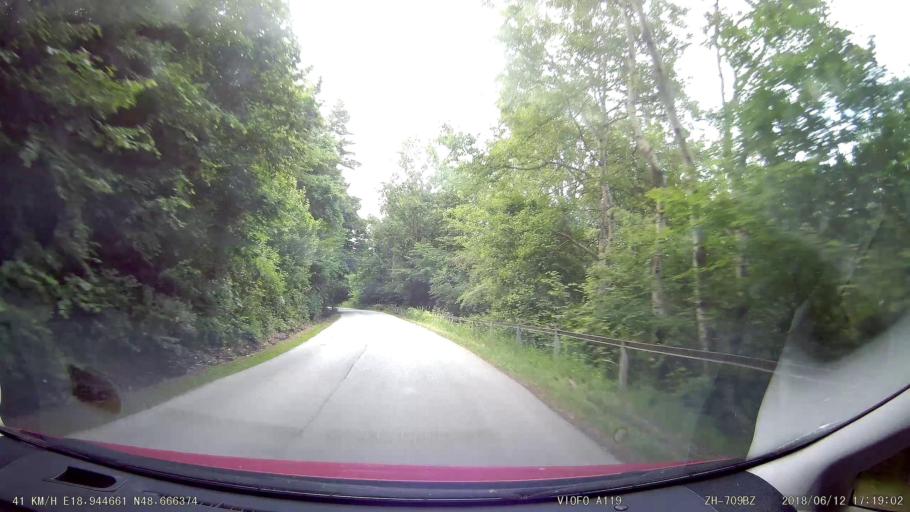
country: SK
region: Banskobystricky
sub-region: Okres Ziar nad Hronom
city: Kremnica
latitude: 48.6666
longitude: 18.9447
